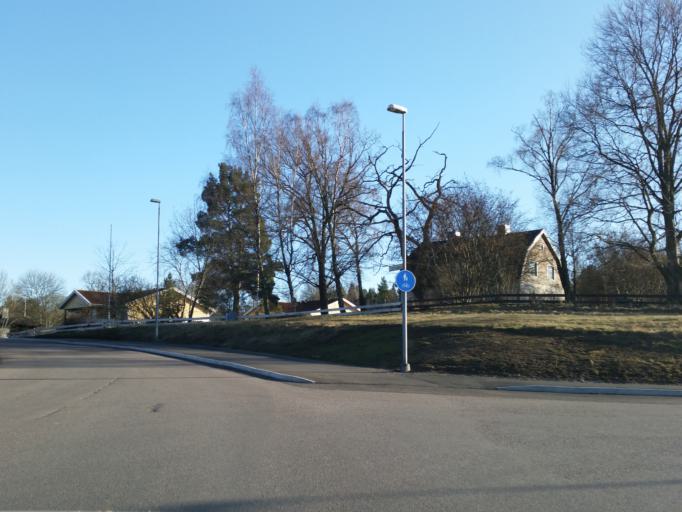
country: SE
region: Kalmar
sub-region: Oskarshamns Kommun
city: Oskarshamn
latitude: 57.2644
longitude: 16.4181
